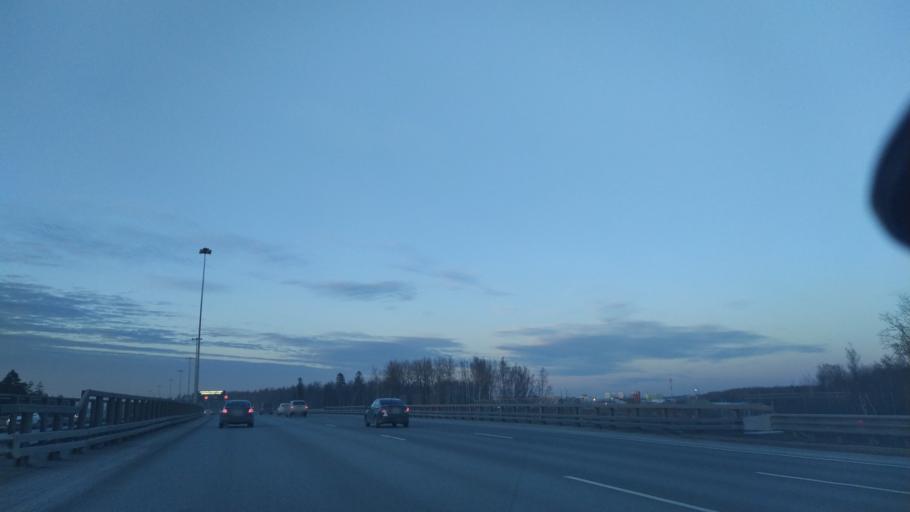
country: RU
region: St.-Petersburg
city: Krasnogvargeisky
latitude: 59.9302
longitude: 30.5361
